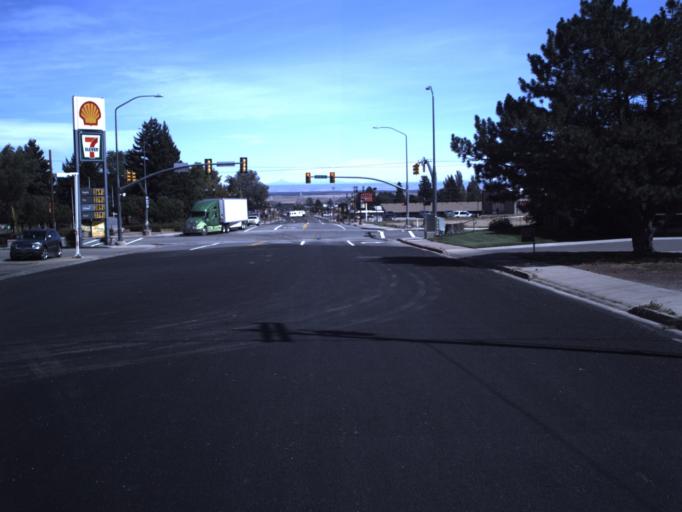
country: US
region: Utah
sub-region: San Juan County
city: Monticello
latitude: 37.8726
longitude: -109.3439
